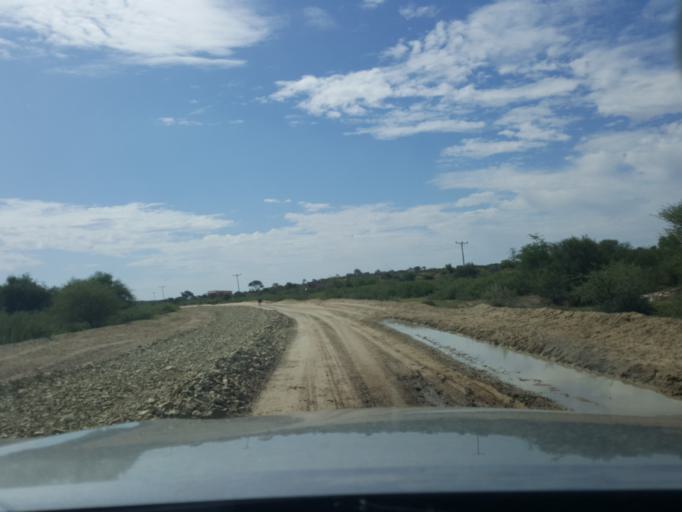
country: BW
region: Kweneng
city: Letlhakeng
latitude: -23.9890
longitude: 24.9719
